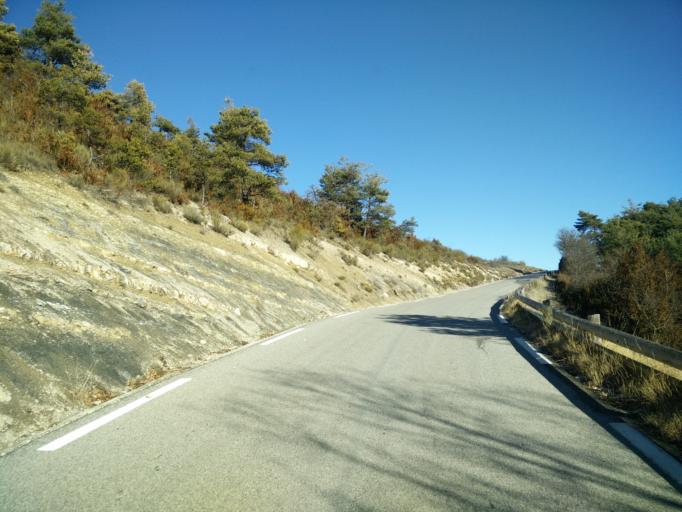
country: FR
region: Provence-Alpes-Cote d'Azur
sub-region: Departement des Alpes-de-Haute-Provence
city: Castellane
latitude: 43.7565
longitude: 6.4385
